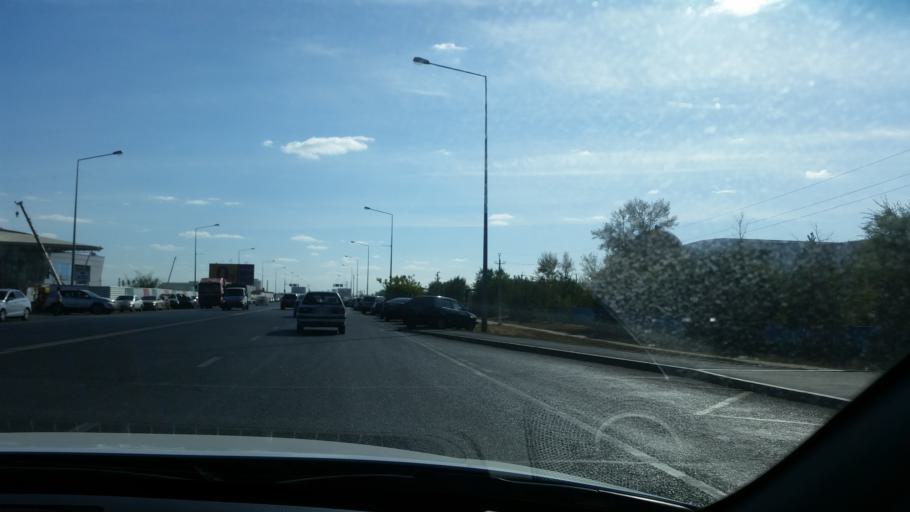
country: KZ
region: Astana Qalasy
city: Astana
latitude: 51.0924
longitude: 71.4036
